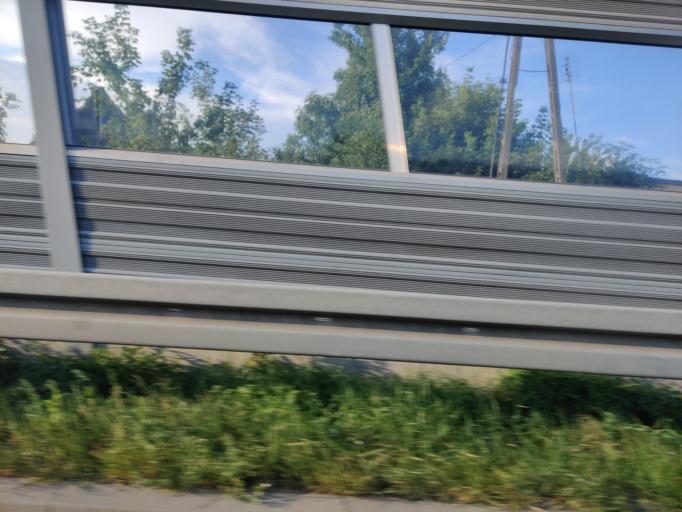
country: PL
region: Greater Poland Voivodeship
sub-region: Konin
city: Konin
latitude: 52.2027
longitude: 18.2744
